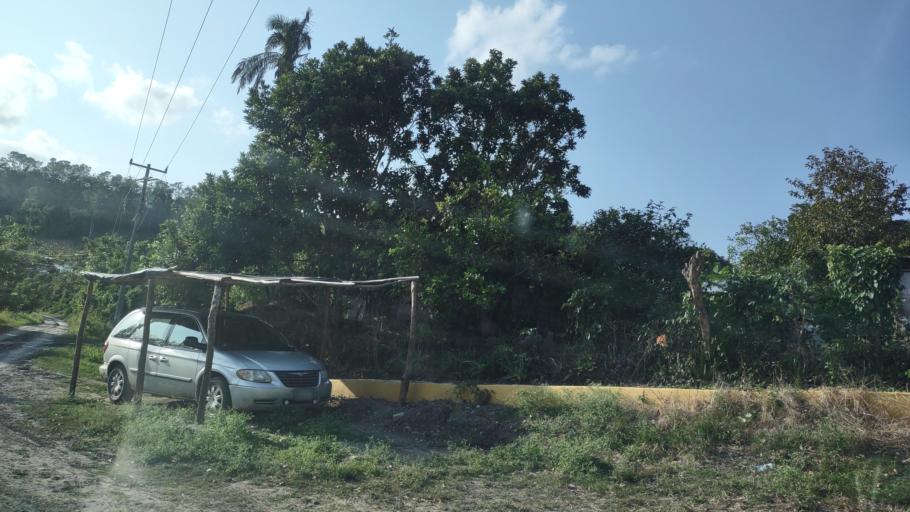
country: MX
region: Veracruz
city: Papantla de Olarte
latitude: 20.4605
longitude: -97.3642
